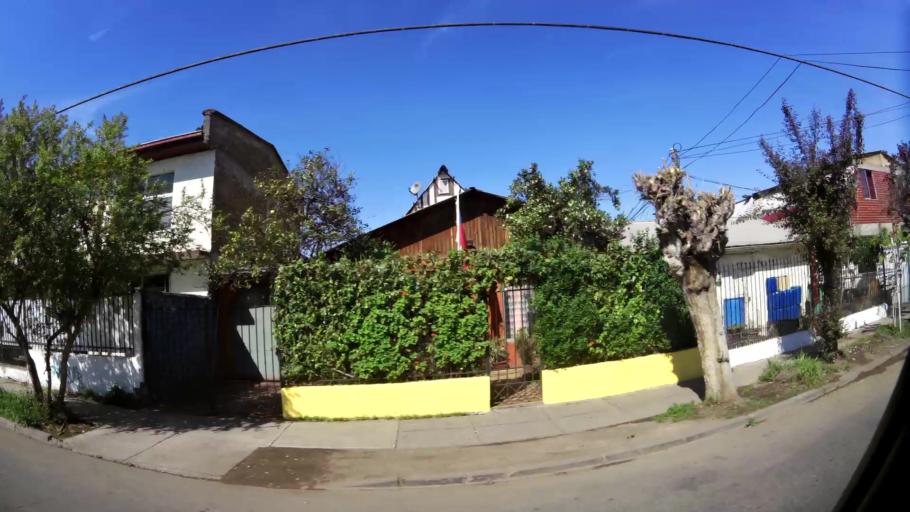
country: CL
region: Santiago Metropolitan
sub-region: Provincia de Santiago
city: Lo Prado
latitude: -33.5013
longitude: -70.7200
